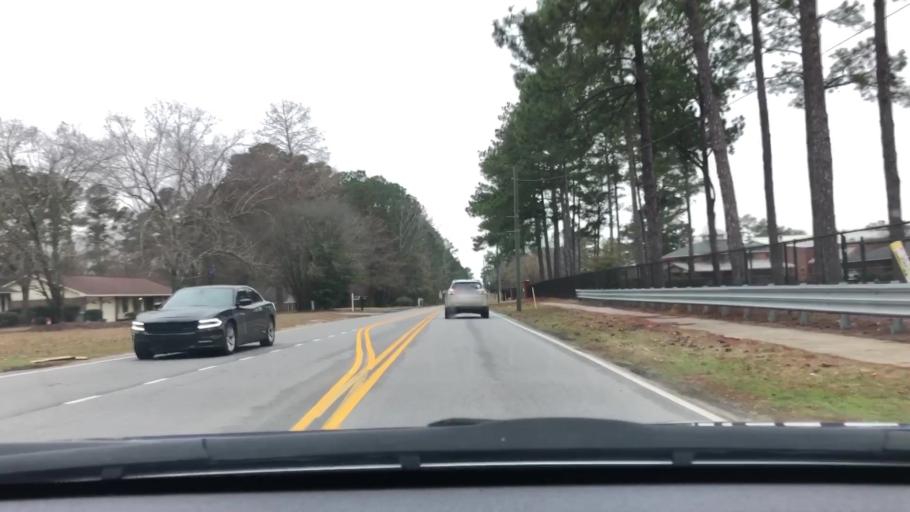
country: US
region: South Carolina
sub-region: Sumter County
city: Cane Savannah
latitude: 33.9346
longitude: -80.4050
